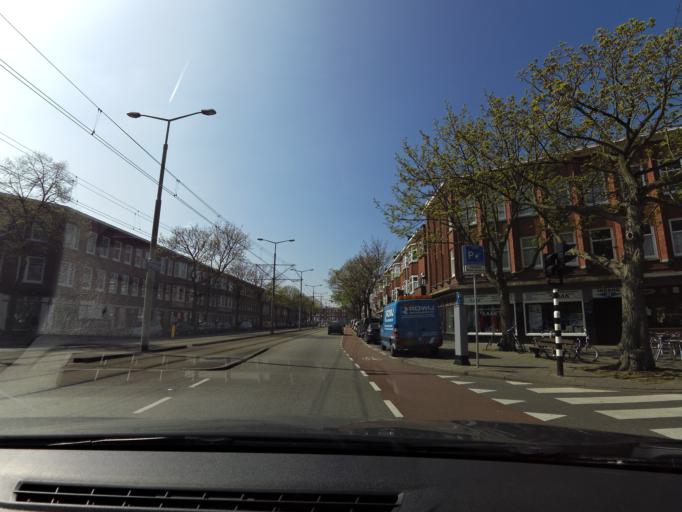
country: NL
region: South Holland
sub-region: Gemeente Rijswijk
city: Rijswijk
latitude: 52.0600
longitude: 4.3313
